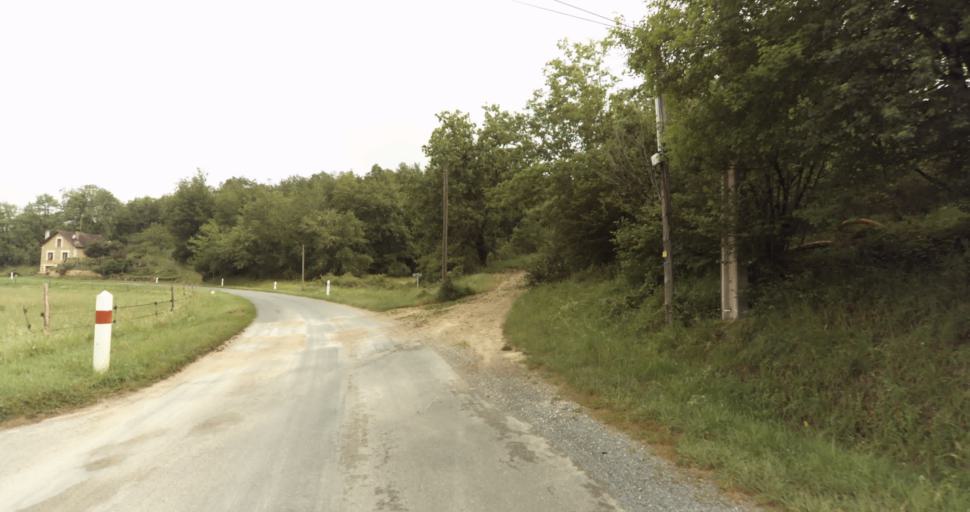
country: FR
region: Aquitaine
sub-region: Departement de la Dordogne
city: Lalinde
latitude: 44.8798
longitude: 0.7785
